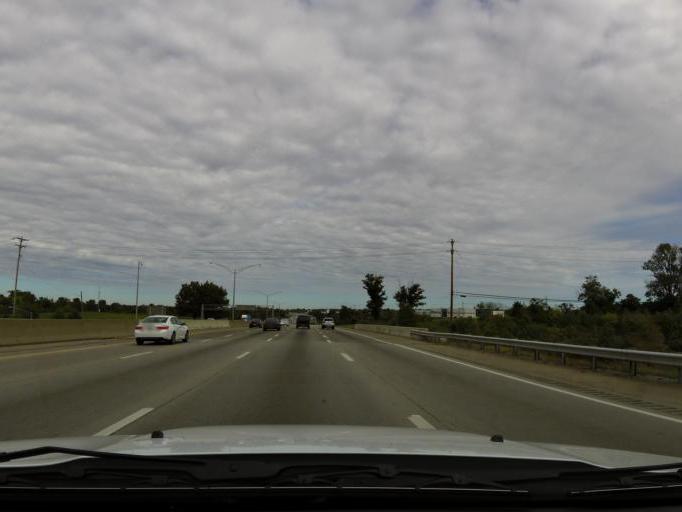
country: US
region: Kentucky
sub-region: Boone County
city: Florence
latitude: 38.9559
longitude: -84.6344
